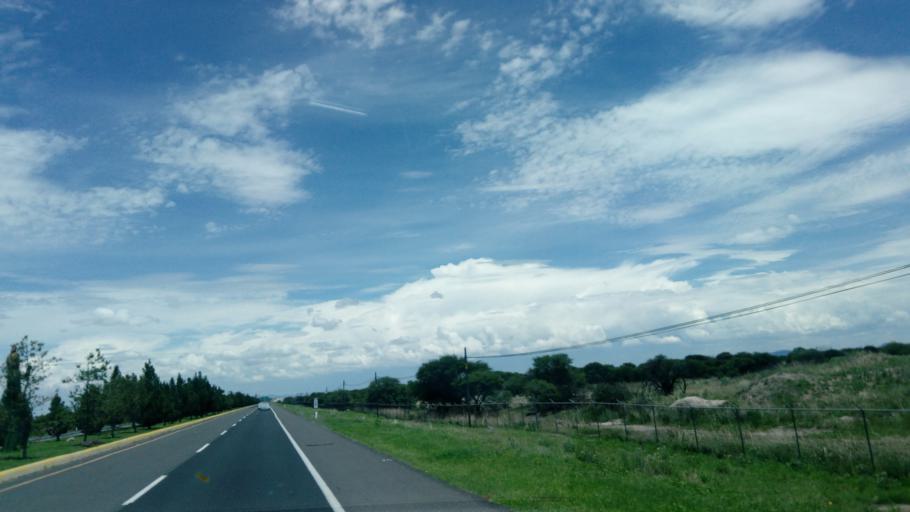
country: MX
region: Durango
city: Victoria de Durango
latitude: 24.1176
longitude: -104.5459
